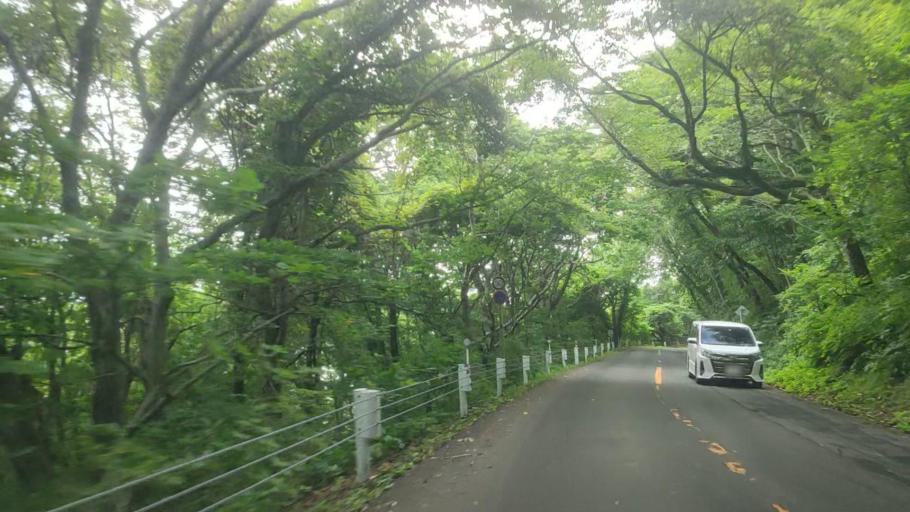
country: JP
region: Hokkaido
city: Hakodate
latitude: 41.7627
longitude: 140.7040
